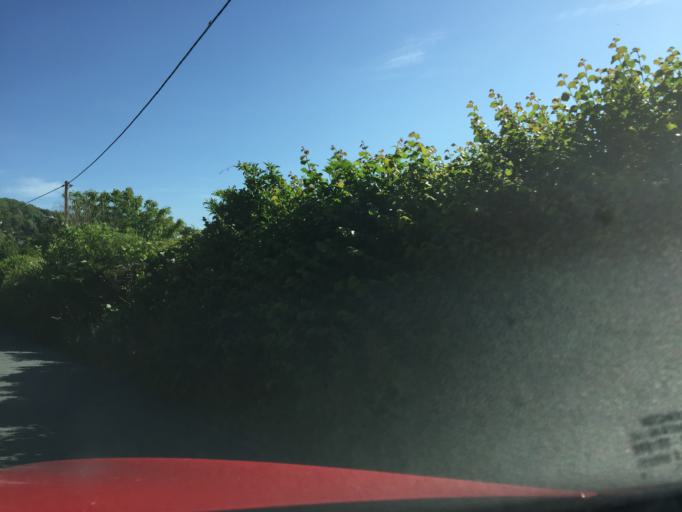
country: GB
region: England
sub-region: Gloucestershire
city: Stonehouse
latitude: 51.7551
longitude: -2.2515
